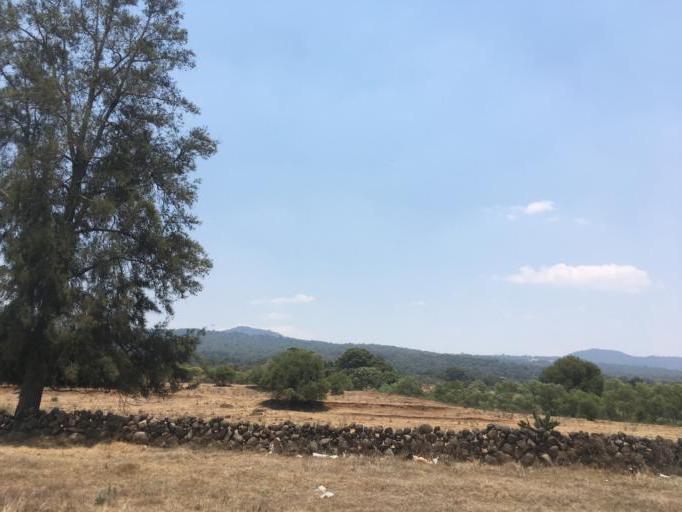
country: MX
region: Michoacan
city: Quiroga
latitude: 19.6502
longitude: -101.4927
